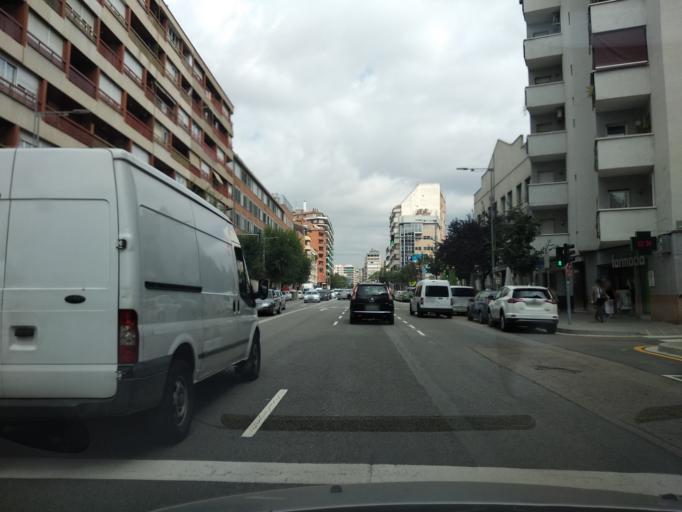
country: ES
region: Catalonia
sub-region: Provincia de Barcelona
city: Granollers
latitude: 41.6039
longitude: 2.2905
